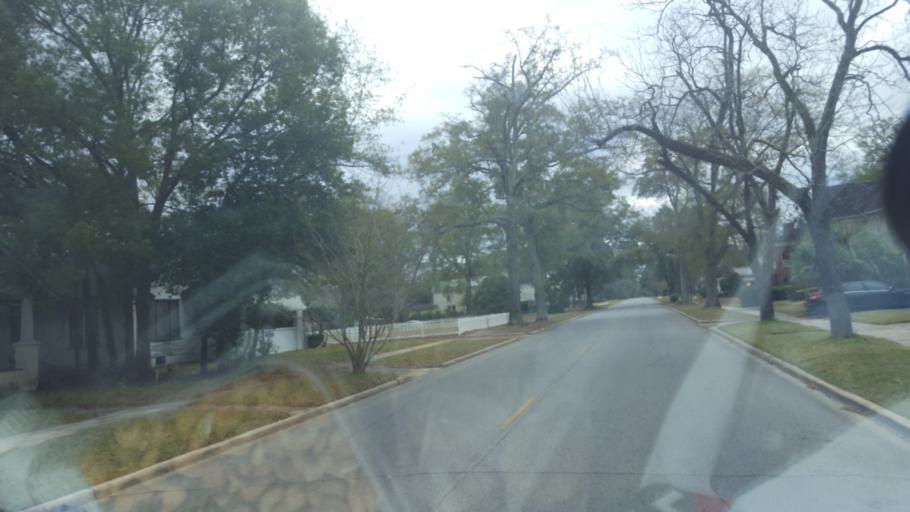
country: US
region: Georgia
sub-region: Ben Hill County
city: Fitzgerald
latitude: 31.7111
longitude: -83.2558
